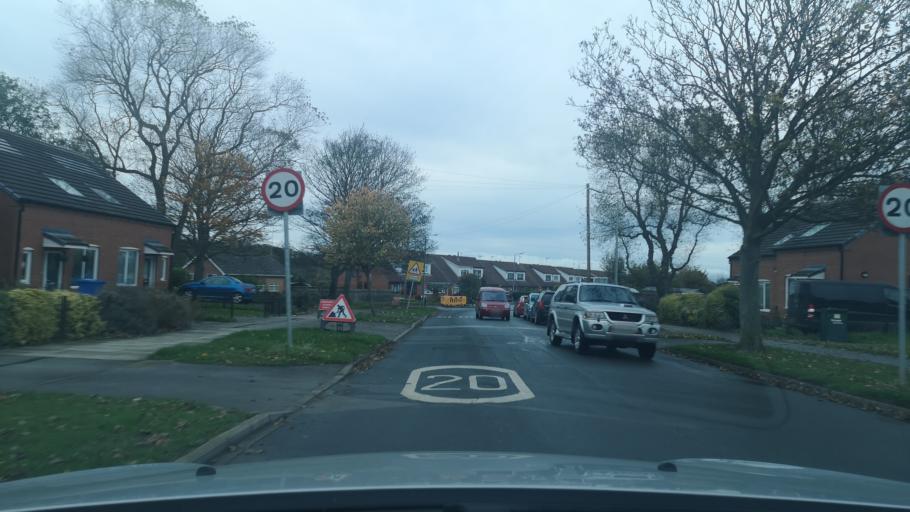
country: GB
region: England
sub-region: East Riding of Yorkshire
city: Hornsea
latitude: 53.9058
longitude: -0.1668
